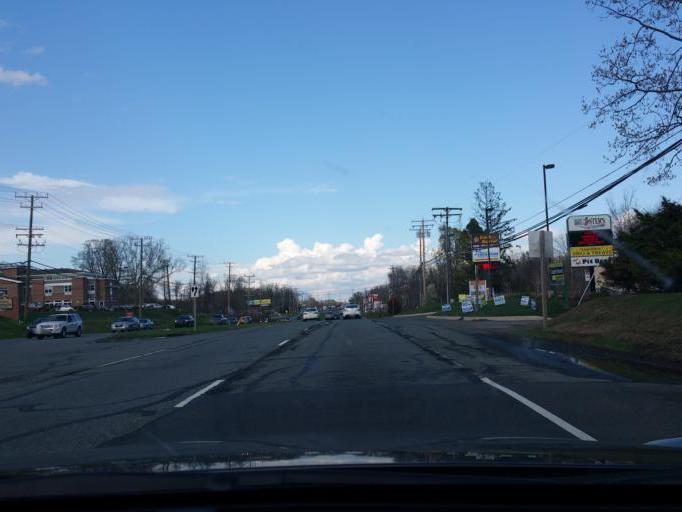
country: US
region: Maryland
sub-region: Harford County
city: Havre de Grace
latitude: 39.5305
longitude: -76.1255
